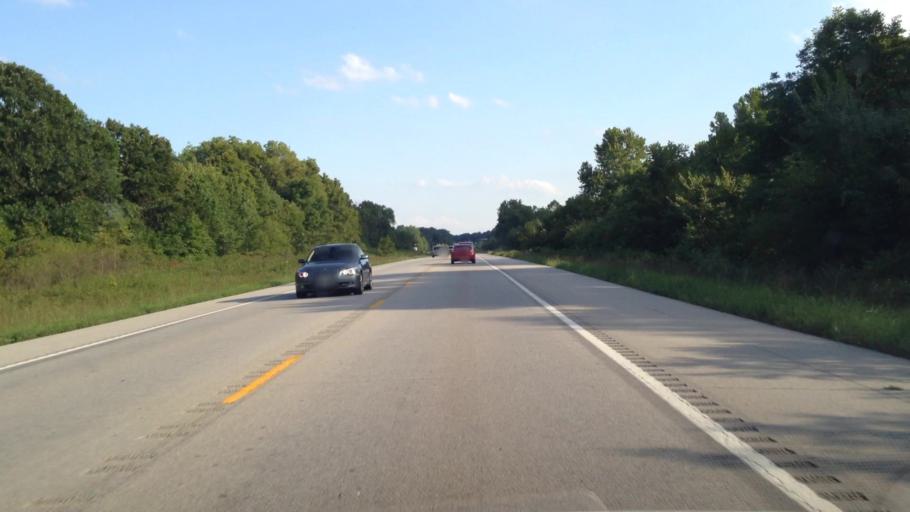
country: US
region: Missouri
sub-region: Jasper County
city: Carl Junction
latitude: 37.1565
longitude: -94.5278
